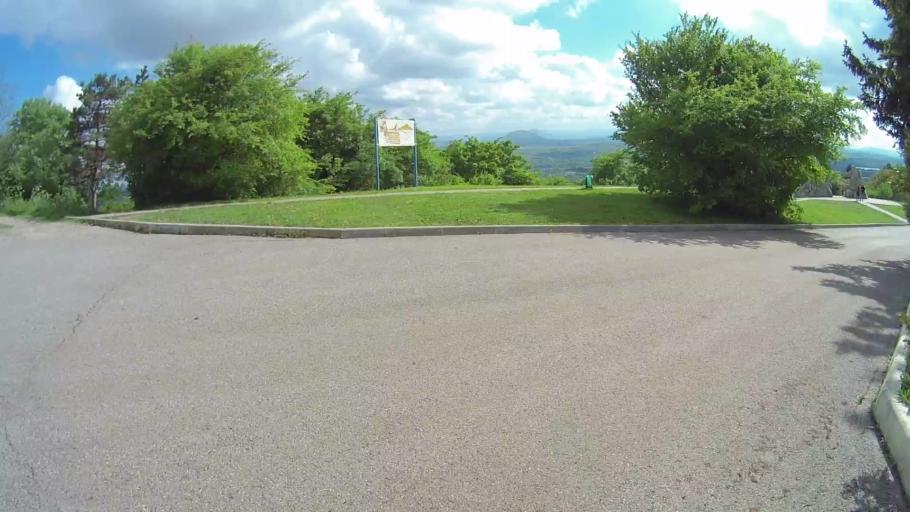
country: RU
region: Stavropol'skiy
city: Pyatigorsk
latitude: 44.0502
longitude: 43.0782
